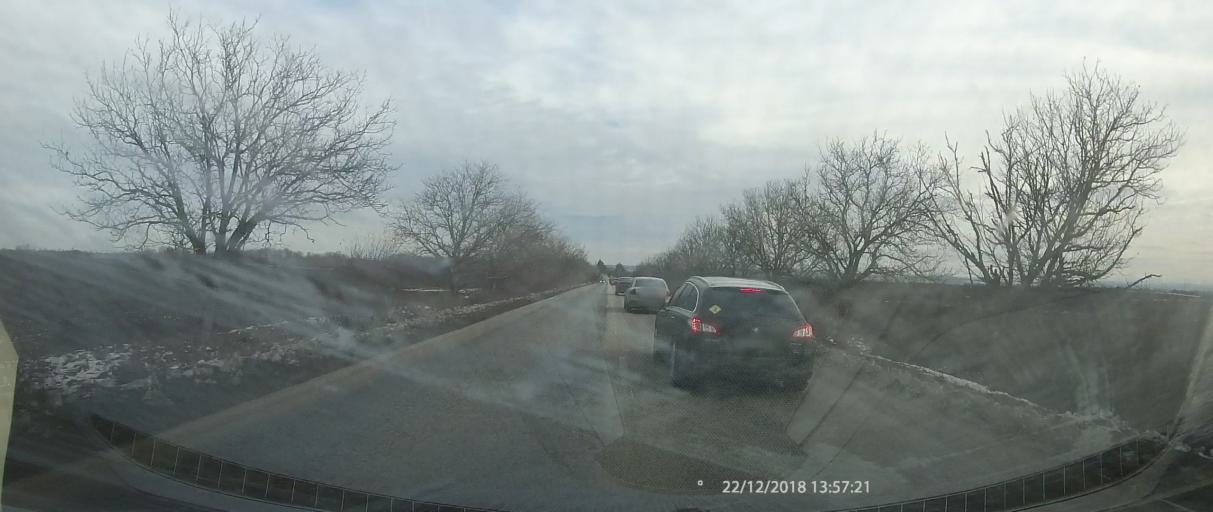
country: BG
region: Pleven
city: Iskur
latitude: 43.3371
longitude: 24.3204
